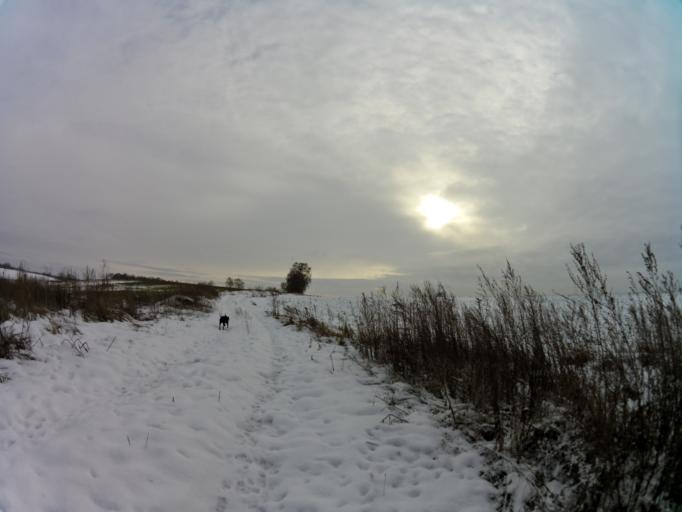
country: PL
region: West Pomeranian Voivodeship
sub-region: Powiat choszczenski
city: Recz
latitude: 53.2812
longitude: 15.5099
